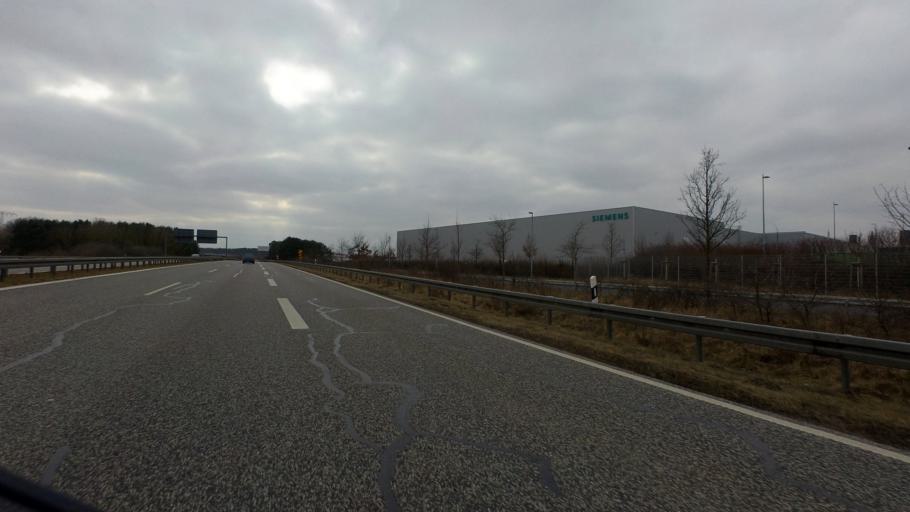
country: DE
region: Brandenburg
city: Ludwigsfelde
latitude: 52.3008
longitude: 13.2850
